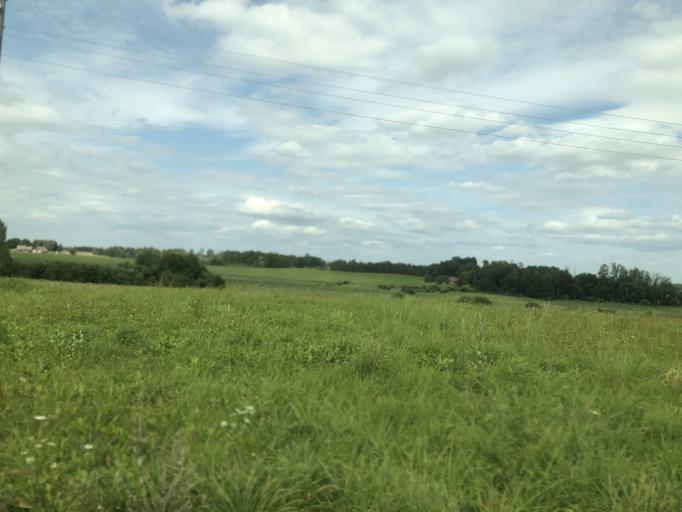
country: LV
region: Vecumnieki
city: Vecumnieki
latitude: 56.4600
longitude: 24.6027
